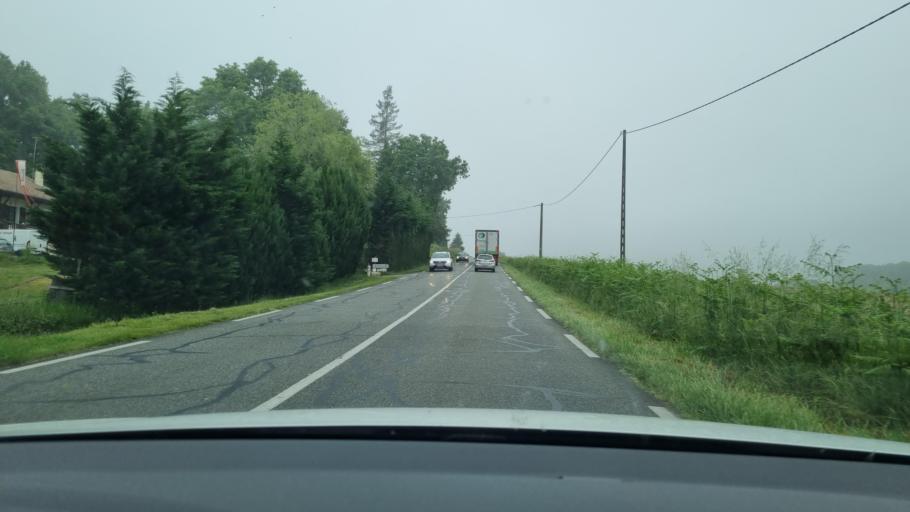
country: FR
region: Aquitaine
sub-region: Departement des Pyrenees-Atlantiques
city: Orthez
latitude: 43.5092
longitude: -0.7320
